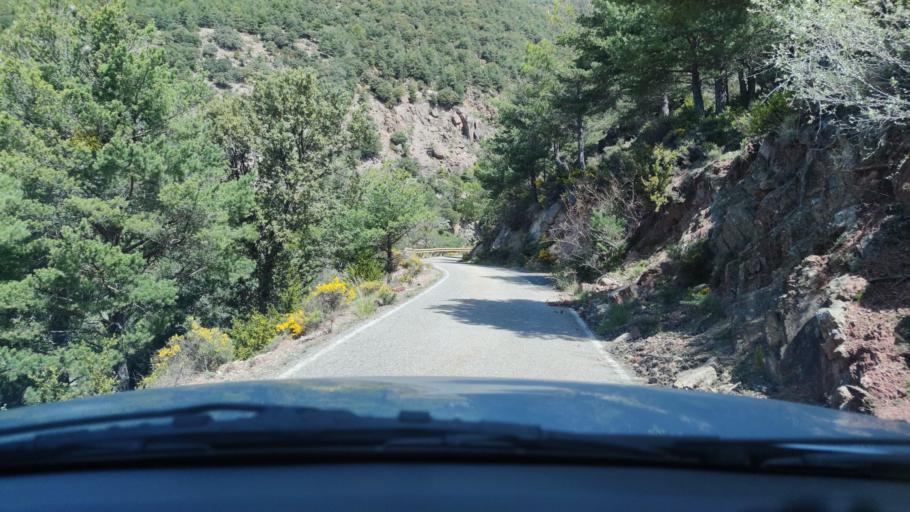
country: ES
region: Catalonia
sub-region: Provincia de Lleida
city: Sort
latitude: 42.3083
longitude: 1.1126
